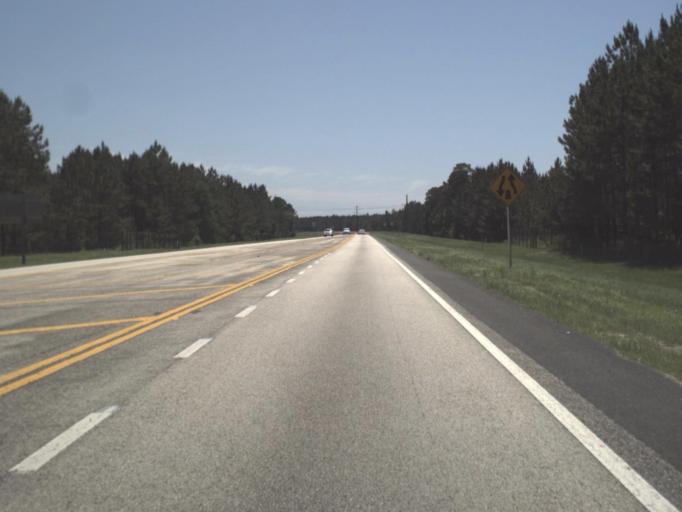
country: US
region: Florida
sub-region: Clay County
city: Lakeside
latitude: 30.1933
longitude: -81.8376
